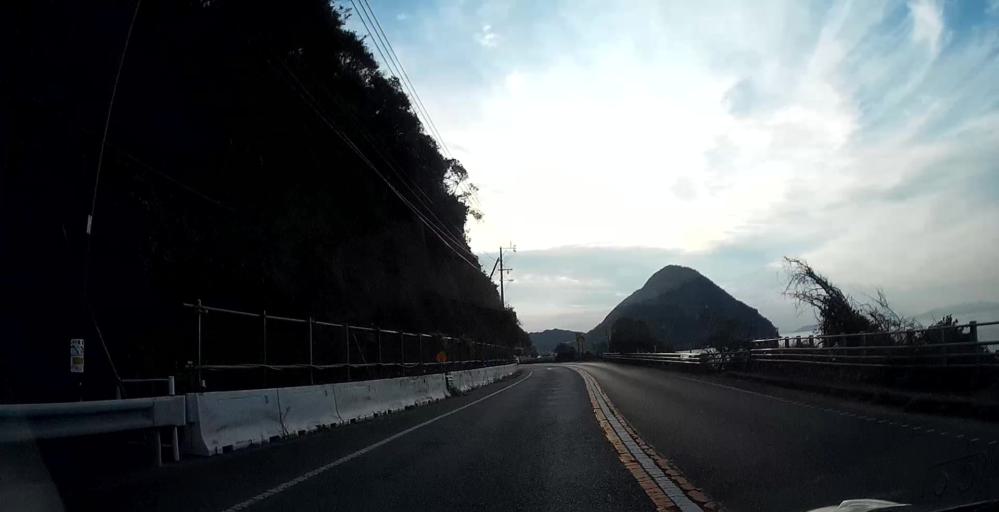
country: JP
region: Nagasaki
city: Shimabara
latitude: 32.6303
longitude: 130.4578
